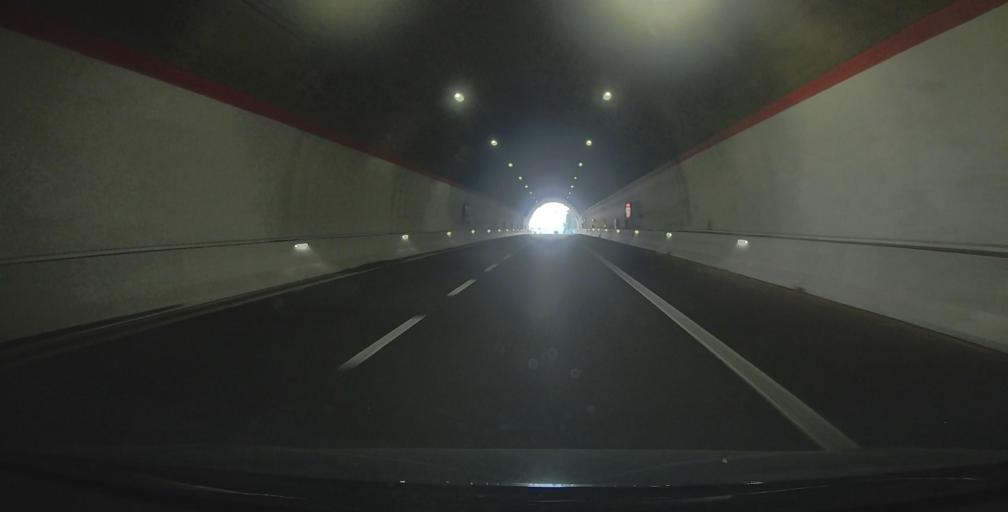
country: IT
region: Calabria
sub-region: Provincia di Cosenza
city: Cosenza
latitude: 39.3065
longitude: 16.2374
